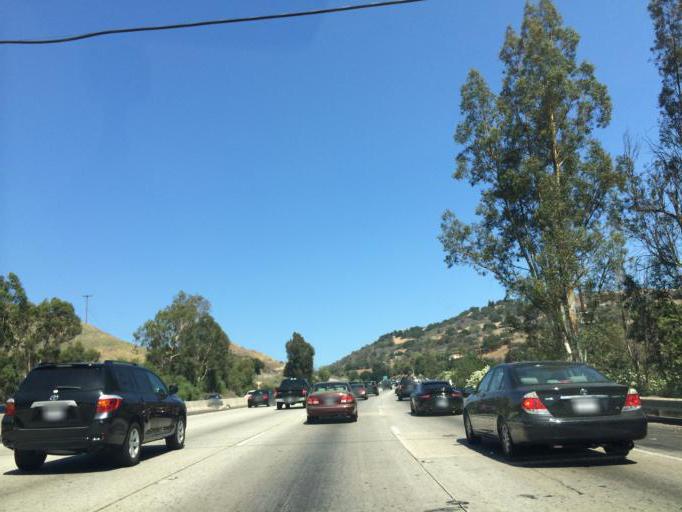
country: US
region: California
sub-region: Los Angeles County
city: Hidden Hills
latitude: 34.1509
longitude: -118.6788
